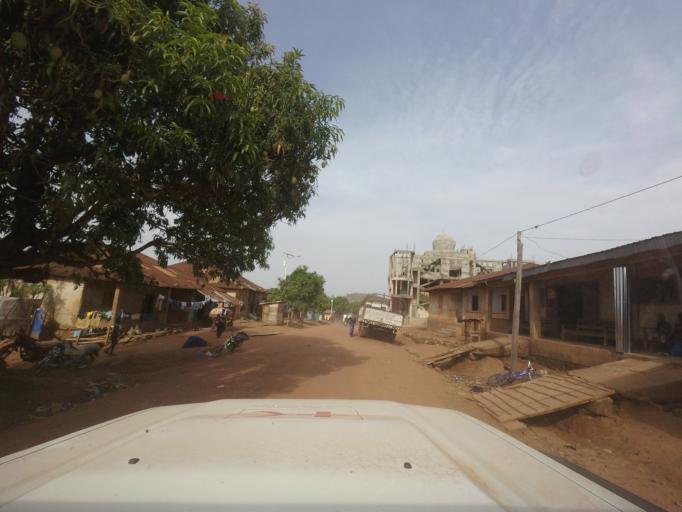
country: GN
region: Nzerekore
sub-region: Prefecture de Guekedou
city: Gueckedou
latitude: 8.5059
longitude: -10.3304
